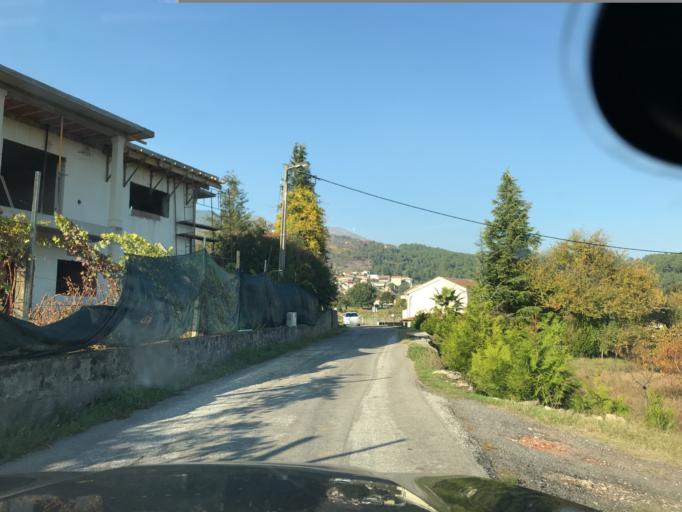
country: PT
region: Vila Real
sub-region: Vila Real
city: Vila Real
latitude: 41.3154
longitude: -7.7590
